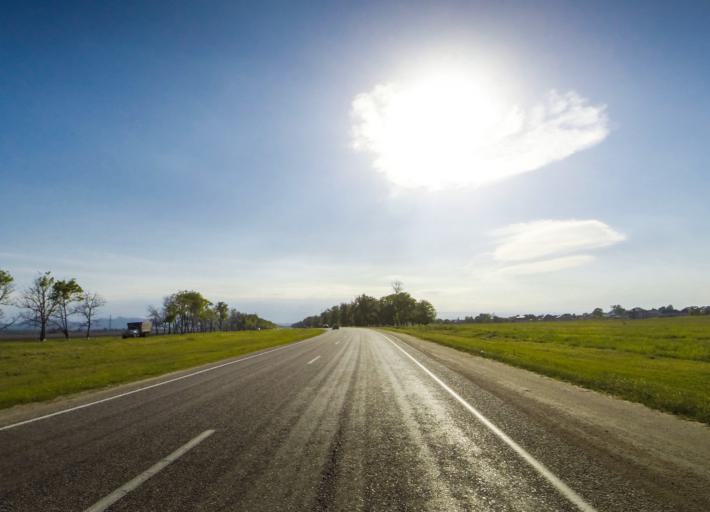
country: RU
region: Kabardino-Balkariya
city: Nartan
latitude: 43.5016
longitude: 43.7183
